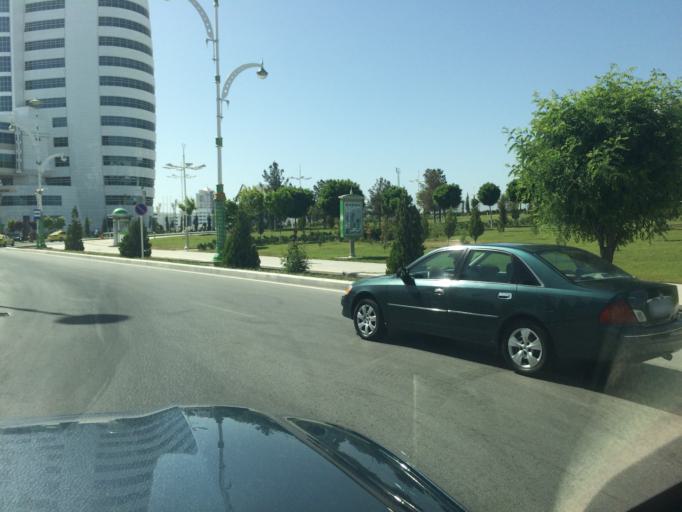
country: TM
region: Ahal
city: Ashgabat
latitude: 37.8966
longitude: 58.3709
